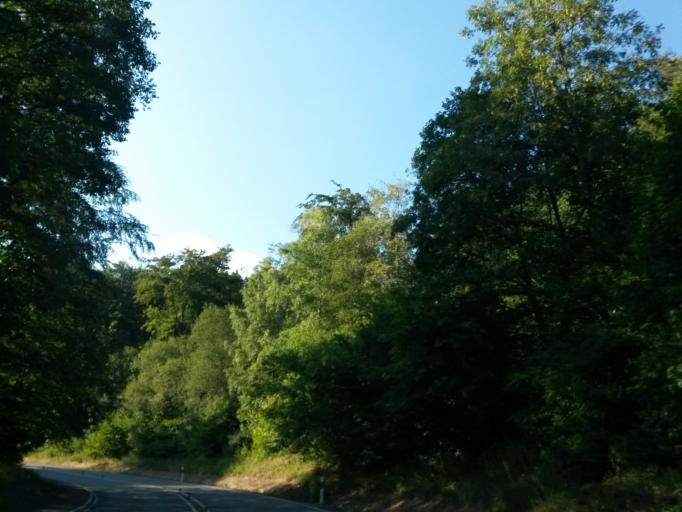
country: DE
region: North Rhine-Westphalia
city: Meinerzhagen
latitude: 51.0914
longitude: 7.6432
